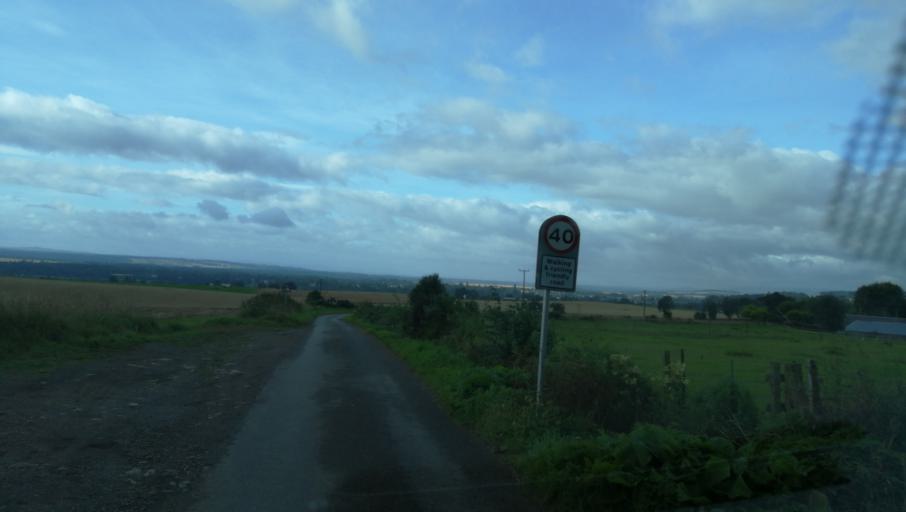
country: GB
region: Scotland
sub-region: Perth and Kinross
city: Blairgowrie
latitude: 56.6048
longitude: -3.3082
